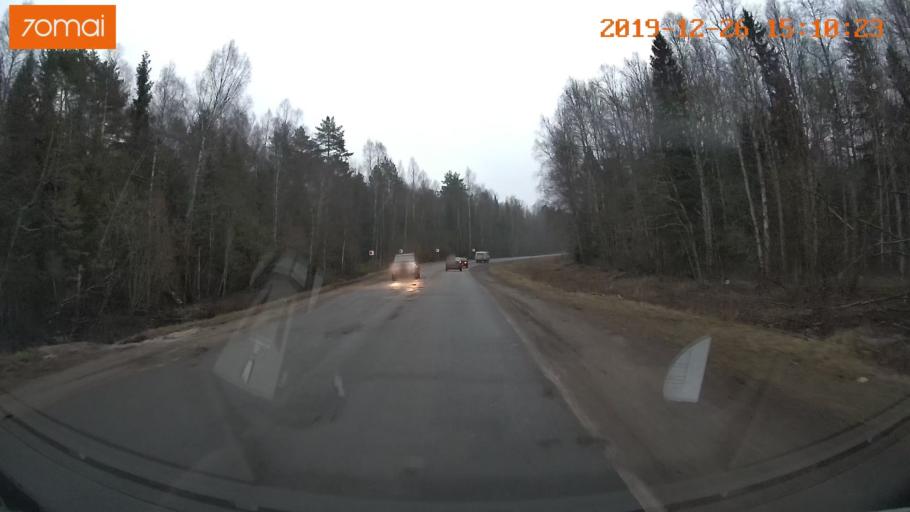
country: RU
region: Jaroslavl
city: Rybinsk
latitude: 58.1407
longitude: 38.8512
